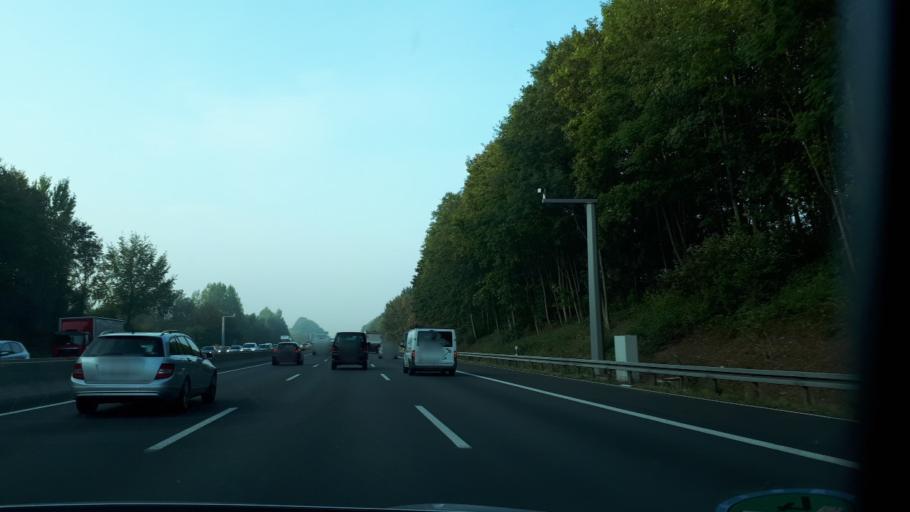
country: DE
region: North Rhine-Westphalia
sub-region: Regierungsbezirk Dusseldorf
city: Erkrath
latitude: 51.2504
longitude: 6.9125
